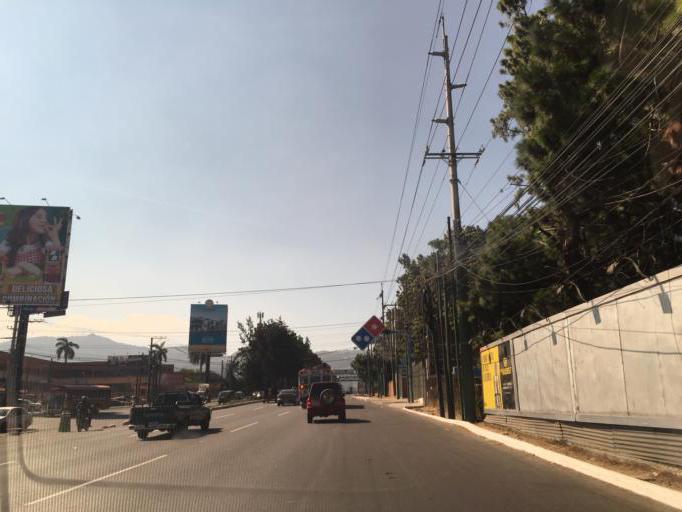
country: GT
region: Guatemala
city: Mixco
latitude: 14.6349
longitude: -90.5912
